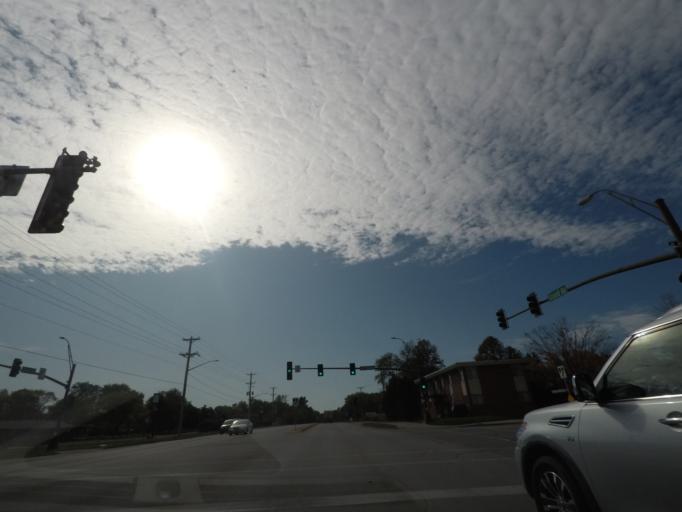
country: US
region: Iowa
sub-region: Story County
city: Ames
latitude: 42.0453
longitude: -93.6210
